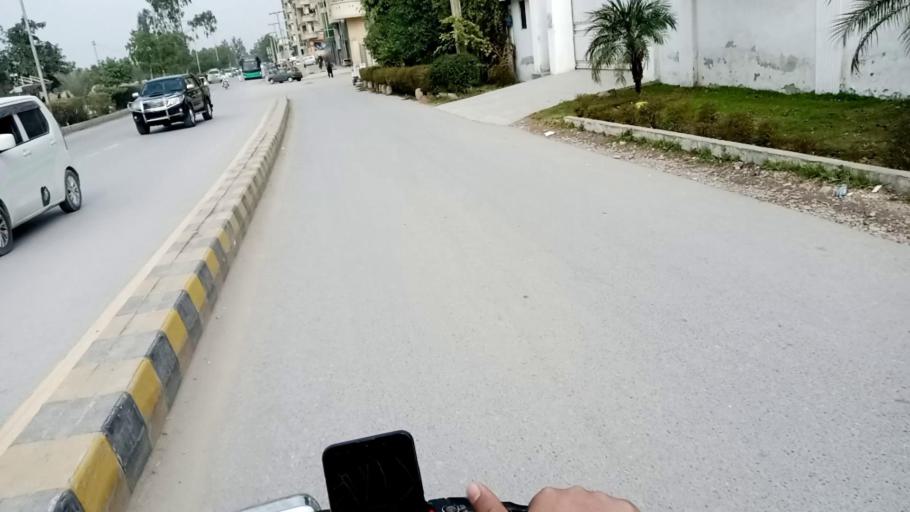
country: PK
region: Khyber Pakhtunkhwa
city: Peshawar
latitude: 33.9689
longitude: 71.4363
